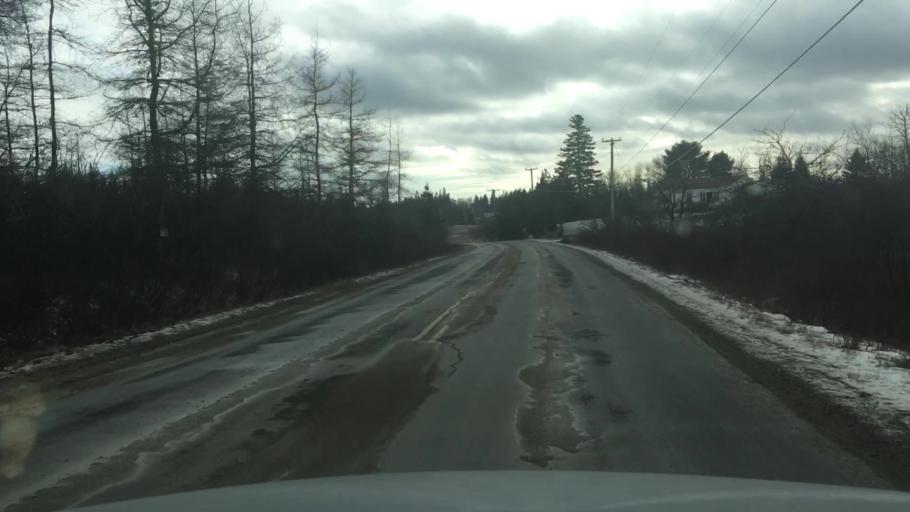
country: US
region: Maine
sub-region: Washington County
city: Machias
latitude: 44.6191
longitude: -67.4798
